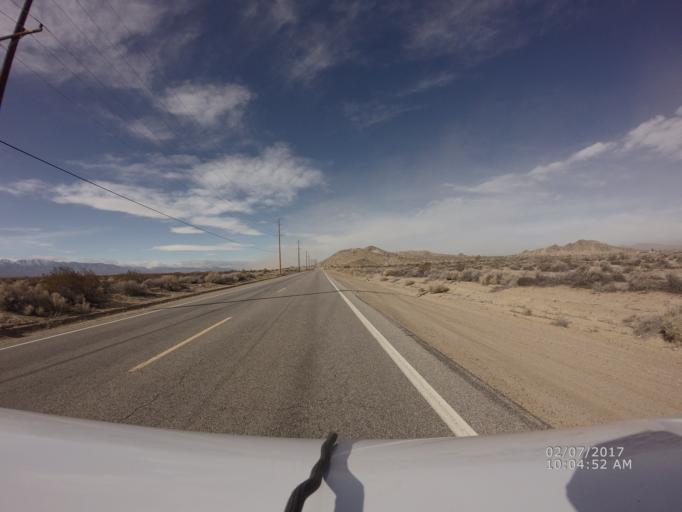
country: US
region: California
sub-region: Los Angeles County
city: Lake Los Angeles
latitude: 34.5798
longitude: -117.7238
